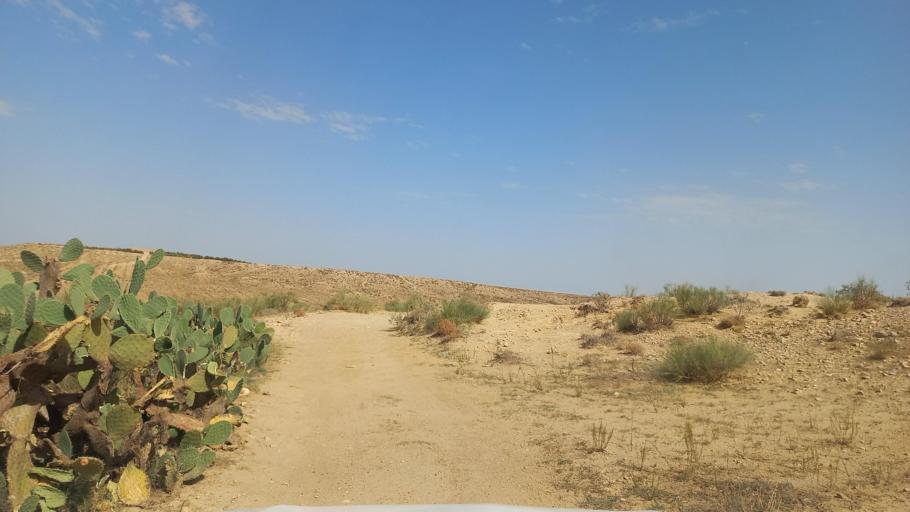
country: TN
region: Al Qasrayn
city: Kasserine
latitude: 35.2789
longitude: 8.9718
